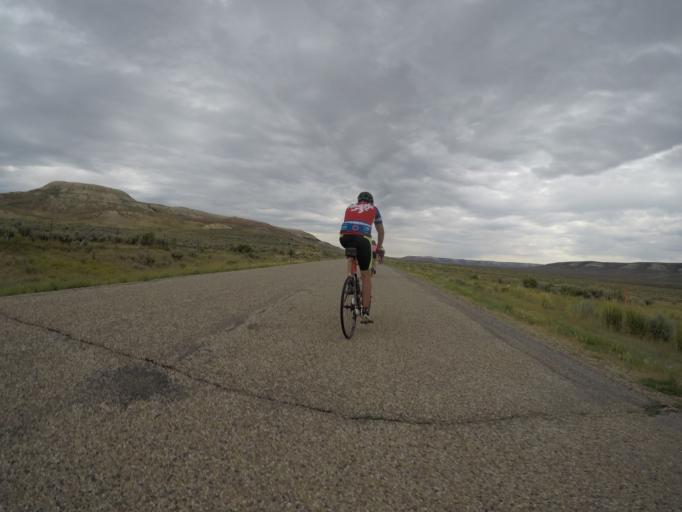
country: US
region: Wyoming
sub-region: Lincoln County
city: Kemmerer
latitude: 41.8230
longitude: -110.7584
